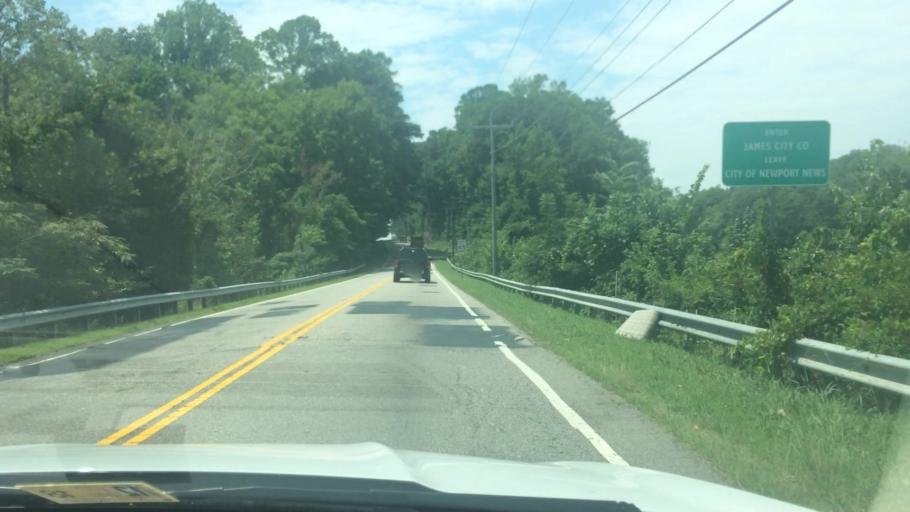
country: US
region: Virginia
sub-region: York County
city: Yorktown
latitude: 37.2094
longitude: -76.5915
